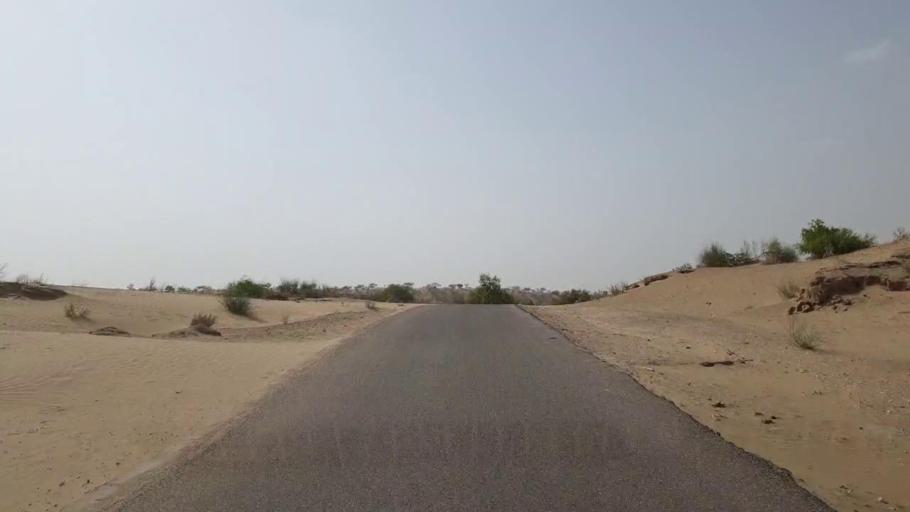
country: PK
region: Sindh
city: Mithi
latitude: 24.5806
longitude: 69.9235
